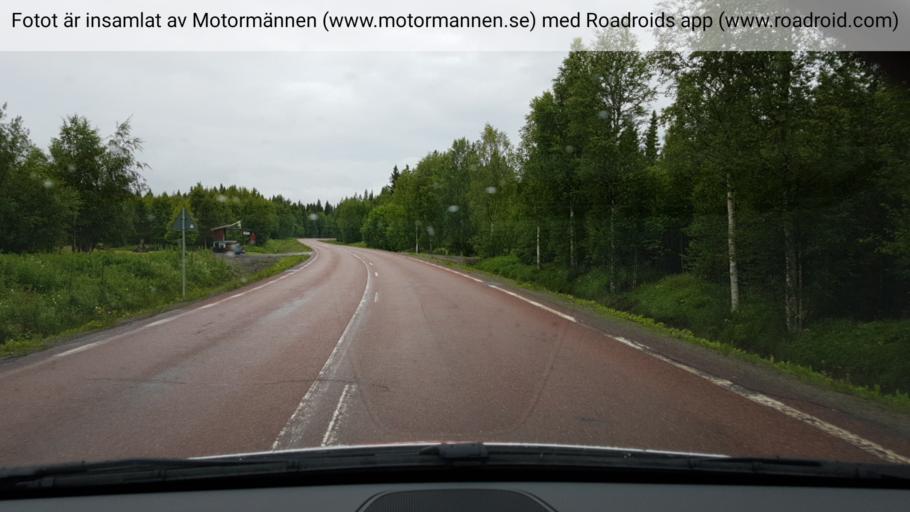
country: SE
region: Jaemtland
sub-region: Stroemsunds Kommun
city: Stroemsund
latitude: 63.9763
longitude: 15.8717
